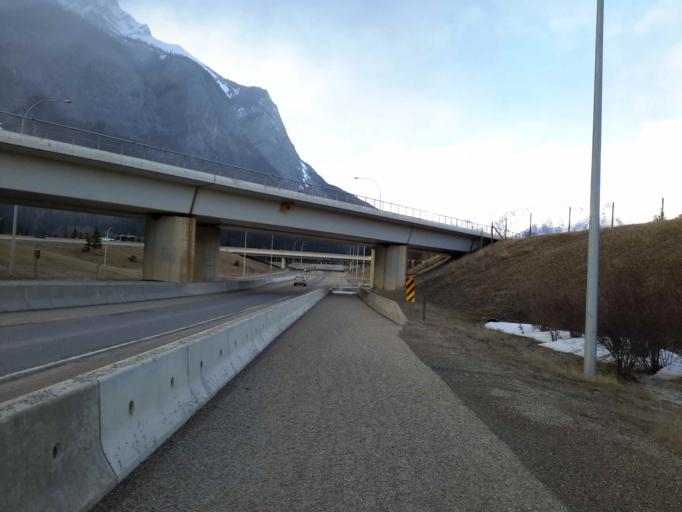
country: CA
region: Alberta
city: Banff
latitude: 51.2056
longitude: -115.5372
